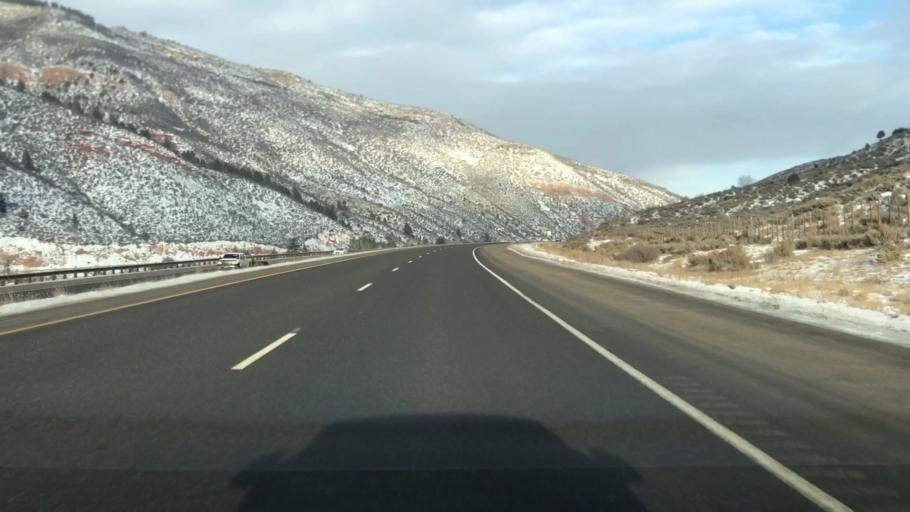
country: US
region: Colorado
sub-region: Eagle County
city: Edwards
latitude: 39.6613
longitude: -106.6397
